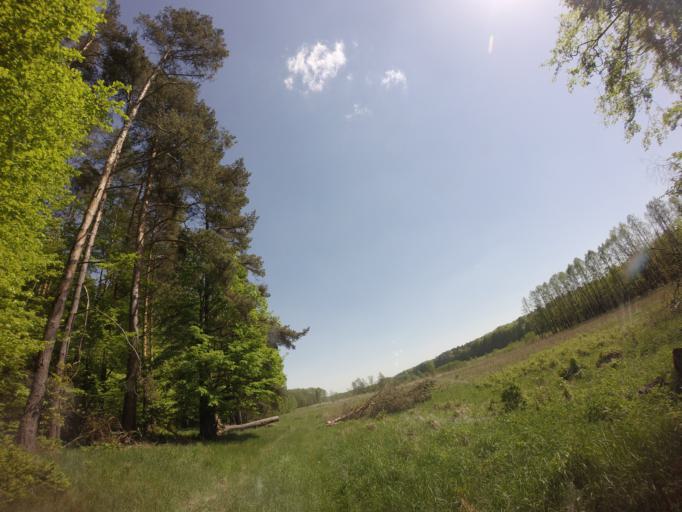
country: PL
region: West Pomeranian Voivodeship
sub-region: Powiat choszczenski
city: Pelczyce
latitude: 52.9502
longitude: 15.3287
